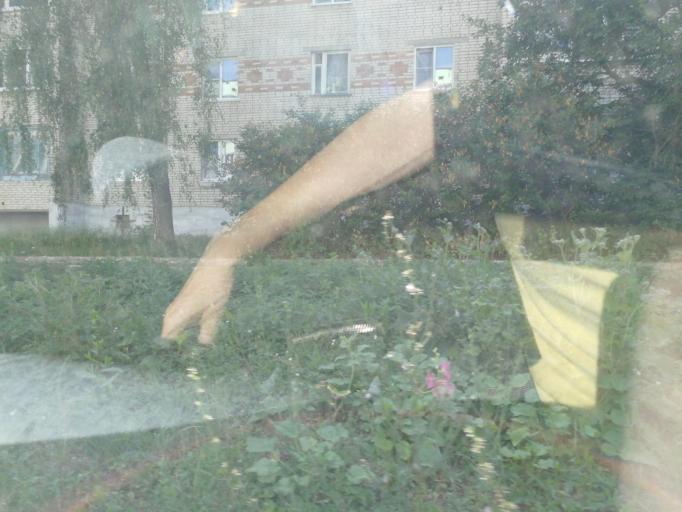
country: RU
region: Tula
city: Bogoroditsk
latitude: 53.7693
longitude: 38.1300
